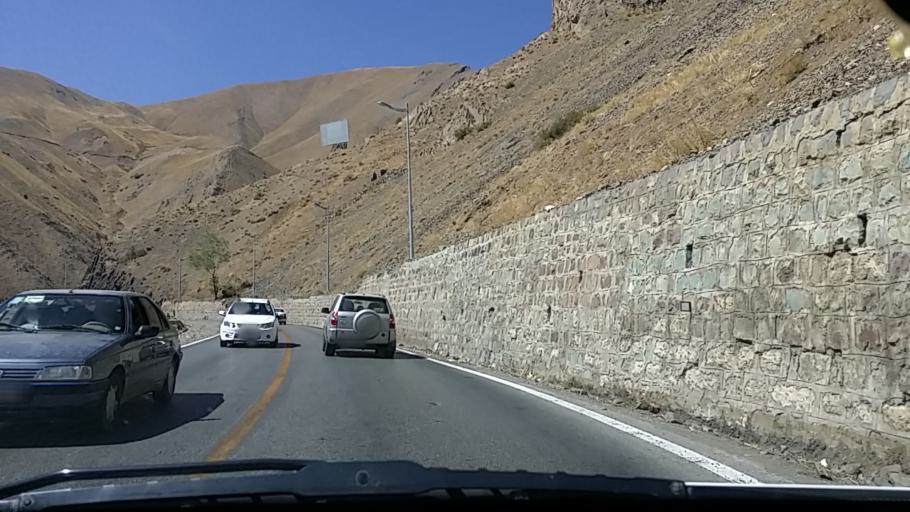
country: IR
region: Tehran
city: Tajrish
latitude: 36.1162
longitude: 51.3227
